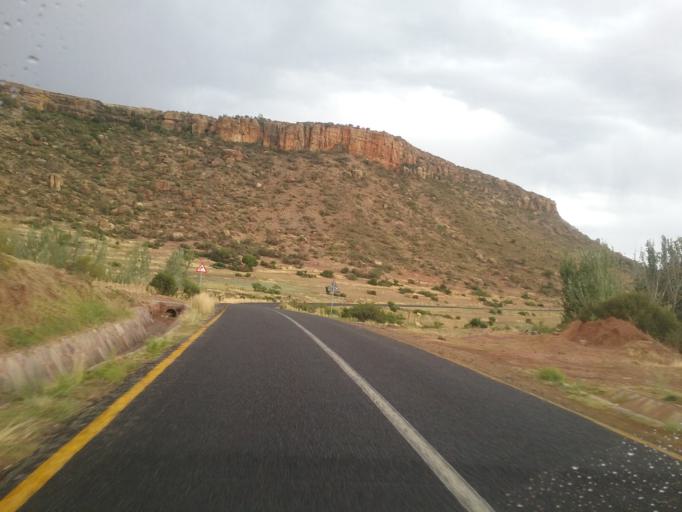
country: LS
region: Quthing
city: Quthing
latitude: -30.3068
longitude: 27.7406
